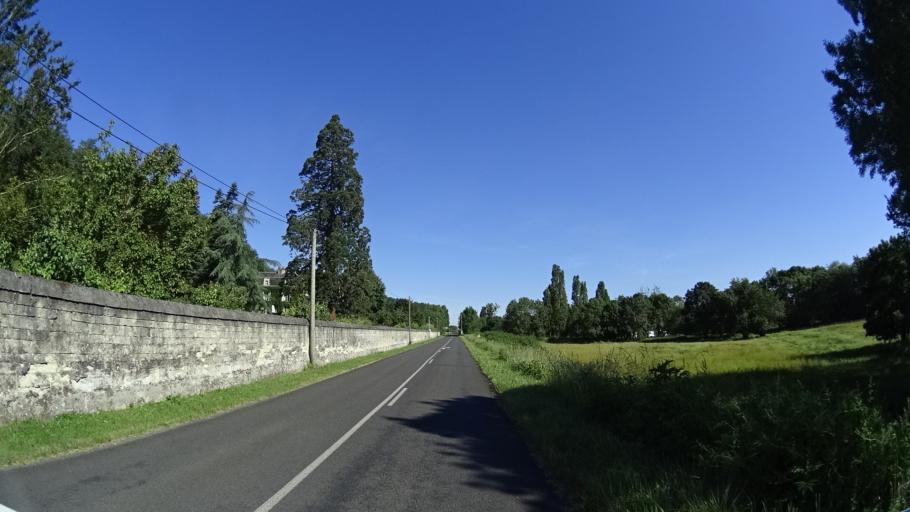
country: FR
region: Pays de la Loire
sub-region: Departement de Maine-et-Loire
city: Saint-Martin-de-la-Place
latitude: 47.2920
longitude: -0.1359
